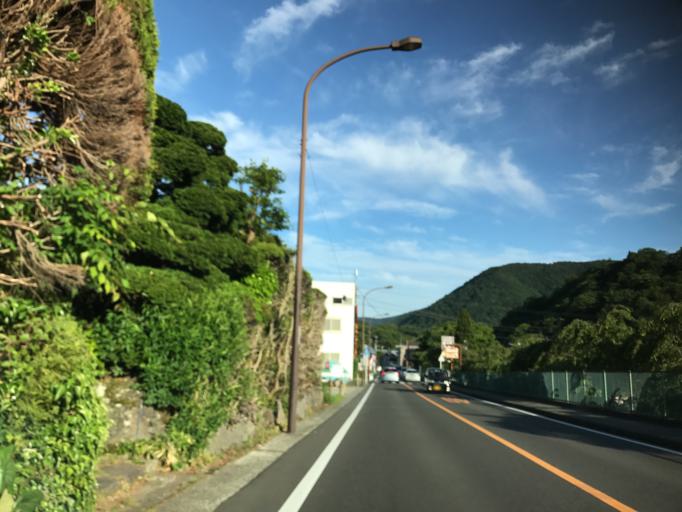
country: JP
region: Kanagawa
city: Hakone
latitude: 35.2561
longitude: 139.0478
